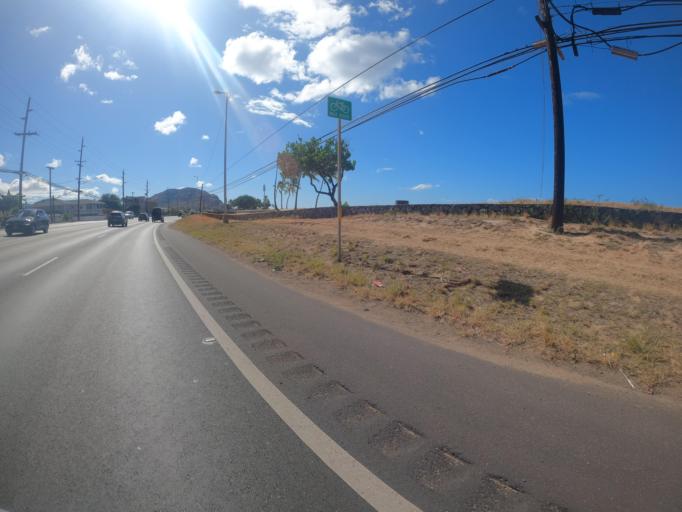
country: US
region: Hawaii
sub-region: Honolulu County
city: Ma'ili
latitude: 21.4279
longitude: -158.1800
